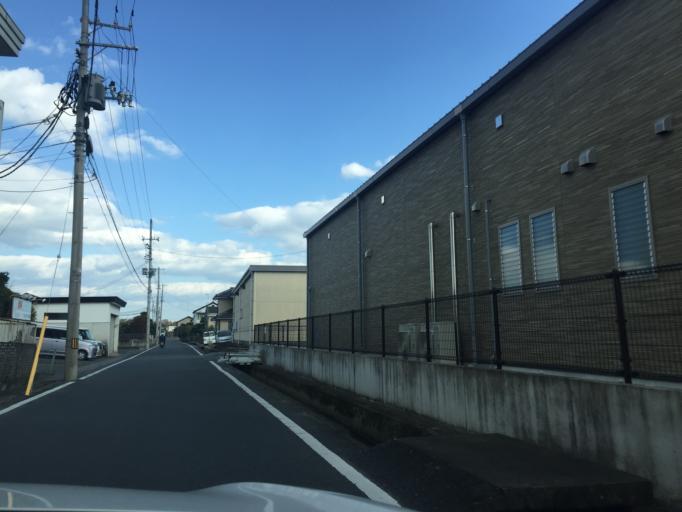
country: JP
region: Fukushima
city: Iwaki
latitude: 37.0593
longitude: 140.8635
